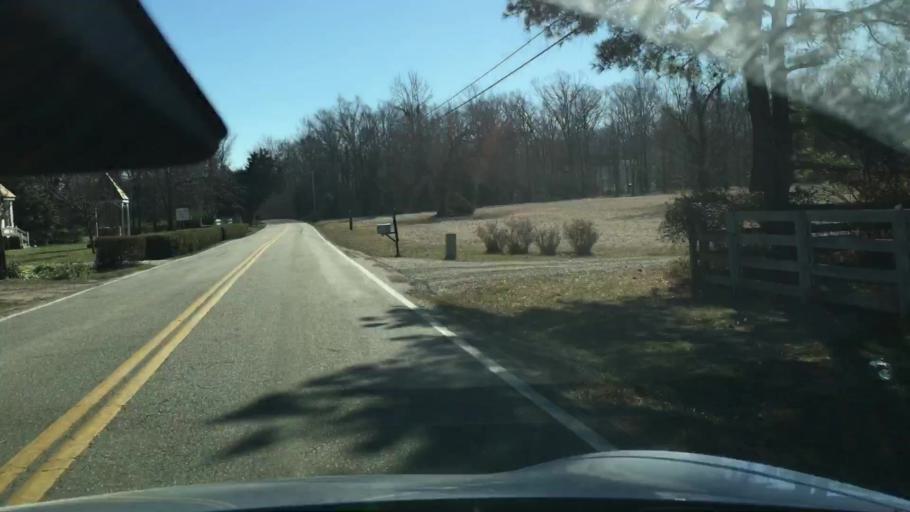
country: US
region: Virginia
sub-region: Henrico County
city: Short Pump
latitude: 37.5902
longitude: -77.7572
